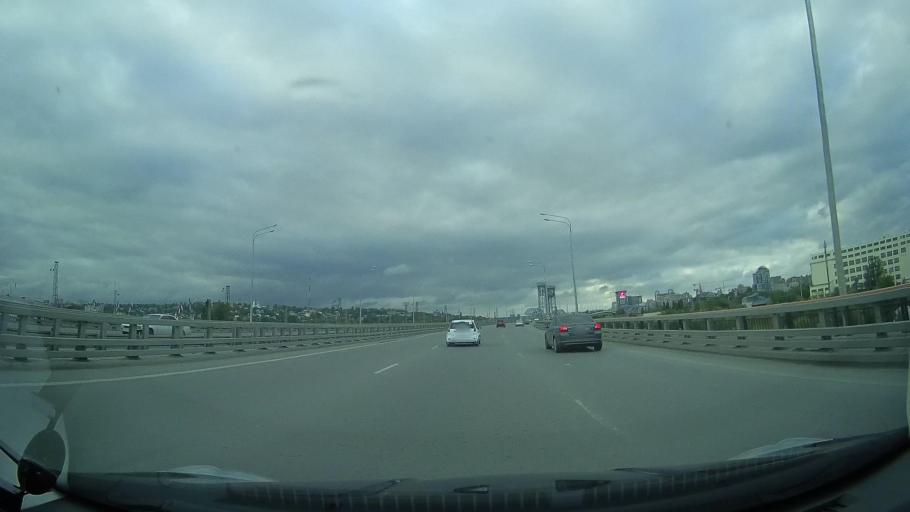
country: RU
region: Rostov
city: Rostov-na-Donu
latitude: 47.2050
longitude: 39.7076
